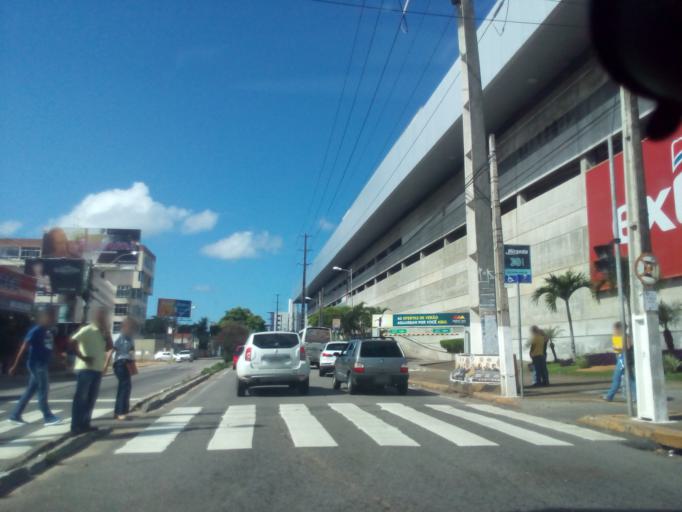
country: BR
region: Rio Grande do Norte
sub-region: Natal
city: Natal
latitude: -5.8116
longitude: -35.2080
